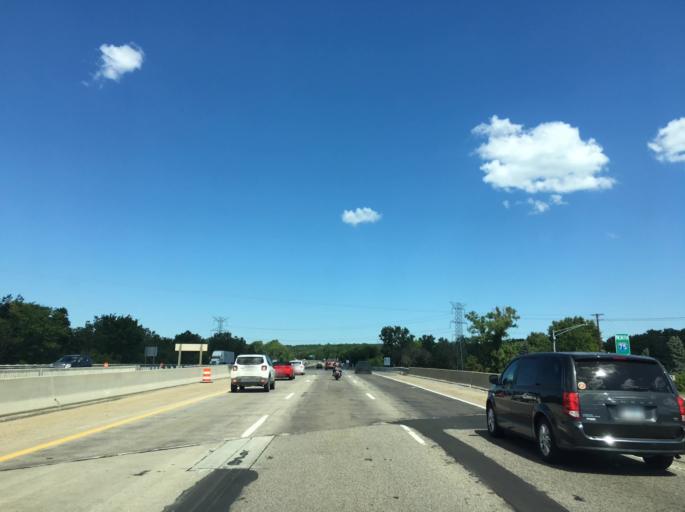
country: US
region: Michigan
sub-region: Oakland County
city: Waterford
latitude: 42.7209
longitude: -83.3490
